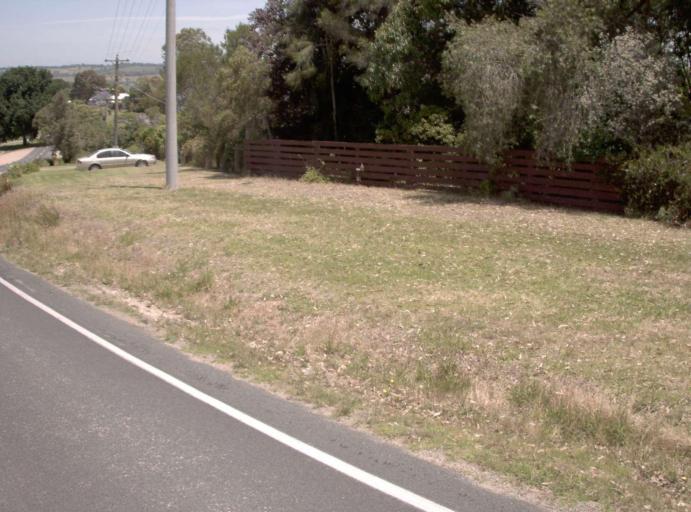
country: AU
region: Victoria
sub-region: East Gippsland
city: Lakes Entrance
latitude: -37.7005
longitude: 147.8358
